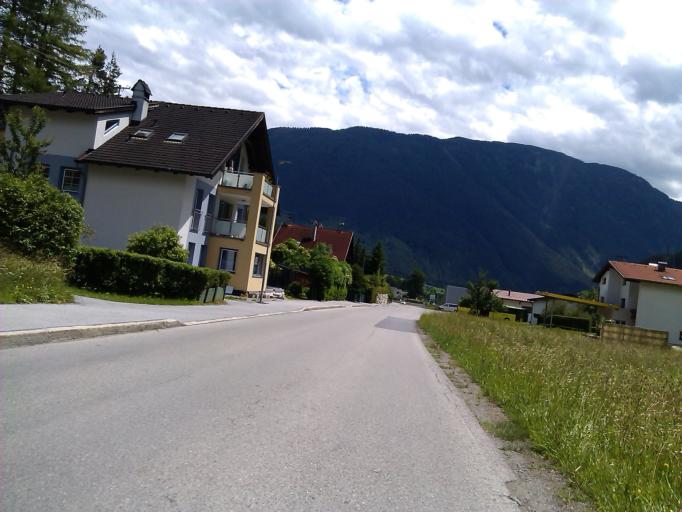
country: AT
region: Tyrol
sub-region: Politischer Bezirk Imst
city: Nassereith
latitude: 47.3193
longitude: 10.8304
